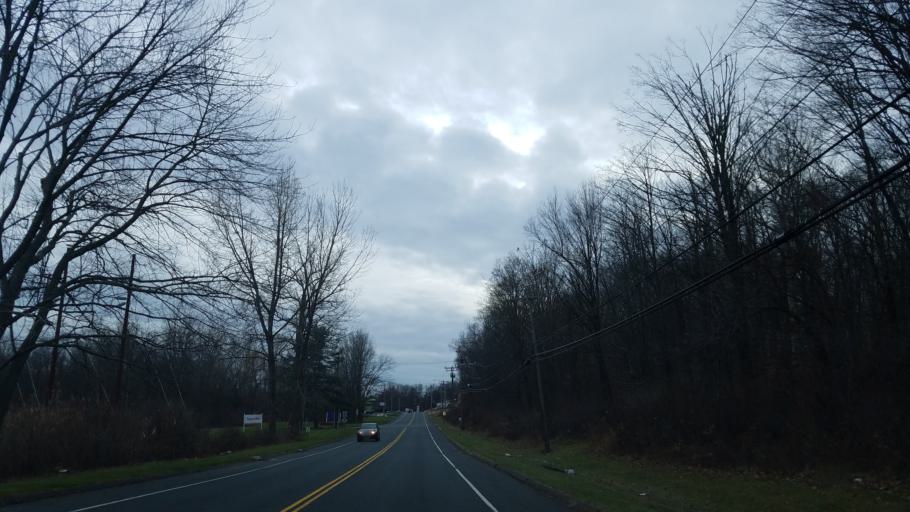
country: US
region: Connecticut
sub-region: Hartford County
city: Newington
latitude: 41.7044
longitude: -72.7520
